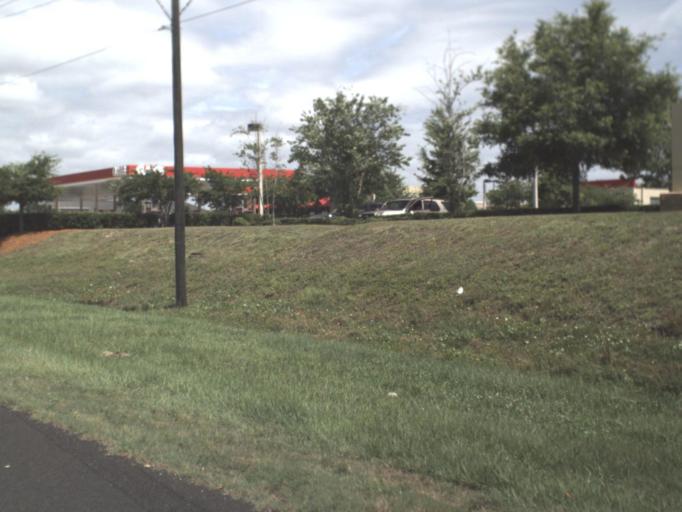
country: US
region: Florida
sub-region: Nassau County
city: Yulee
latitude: 30.6265
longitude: -81.5486
